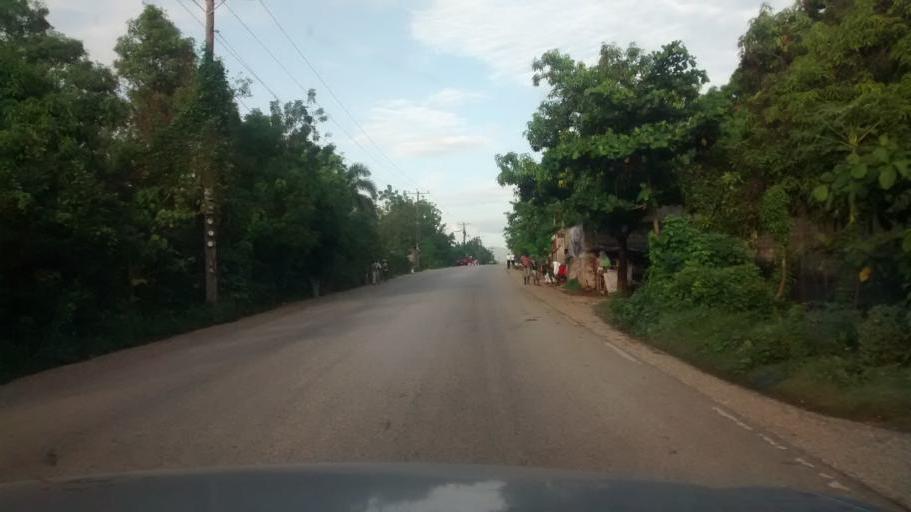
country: HT
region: Nippes
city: Miragoane
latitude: 18.4237
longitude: -73.0175
